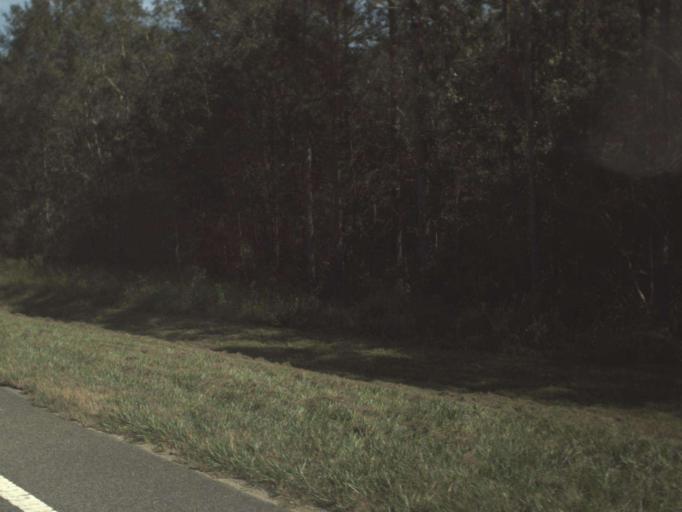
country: US
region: Florida
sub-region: Washington County
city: Chipley
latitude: 30.6969
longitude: -85.5638
